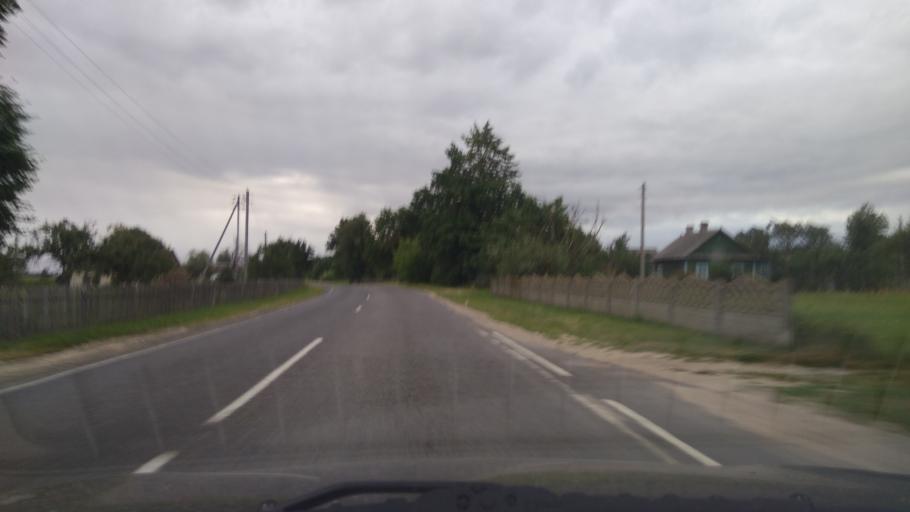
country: BY
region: Brest
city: Byaroza
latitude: 52.4226
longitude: 24.9810
